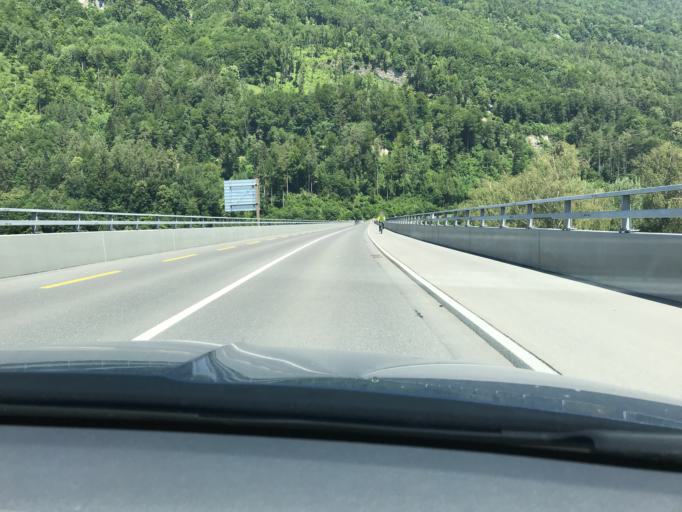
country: CH
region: Bern
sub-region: Interlaken-Oberhasli District
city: Interlaken
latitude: 46.6913
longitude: 7.8727
